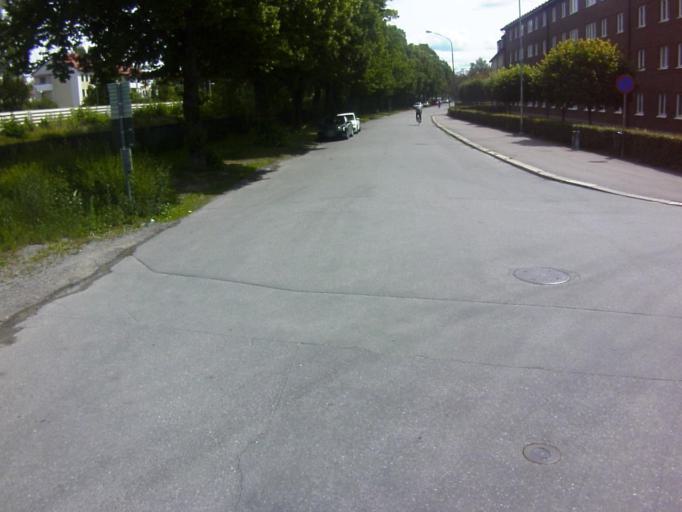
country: SE
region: Soedermanland
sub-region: Eskilstuna Kommun
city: Eskilstuna
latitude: 59.3653
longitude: 16.5228
